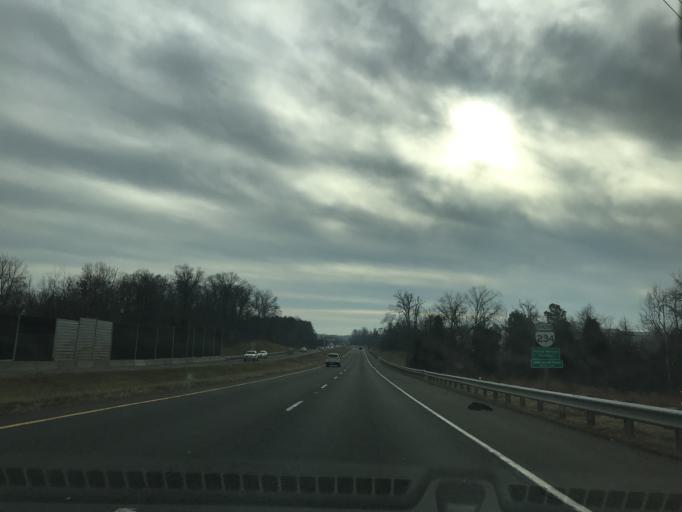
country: US
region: Virginia
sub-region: City of Manassas
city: Manassas
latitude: 38.7305
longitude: -77.5062
